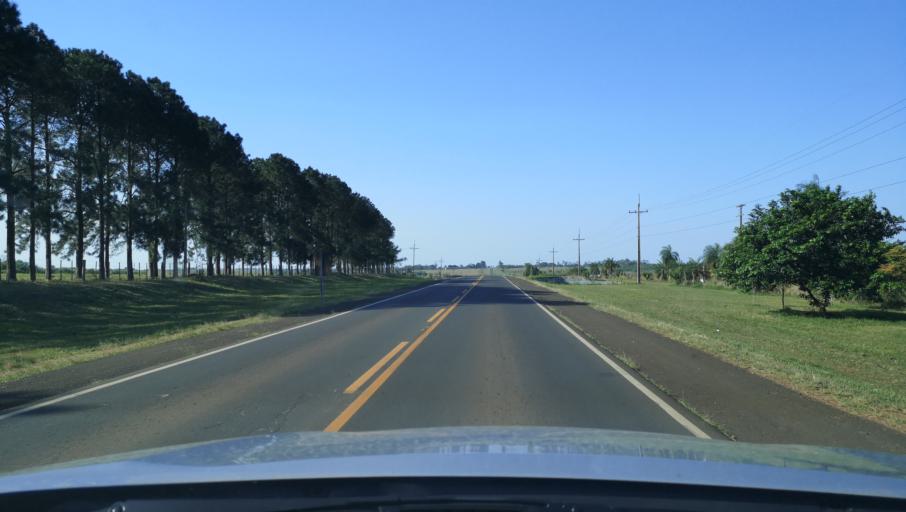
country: PY
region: Misiones
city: Santa Maria
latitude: -26.8407
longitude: -57.0361
